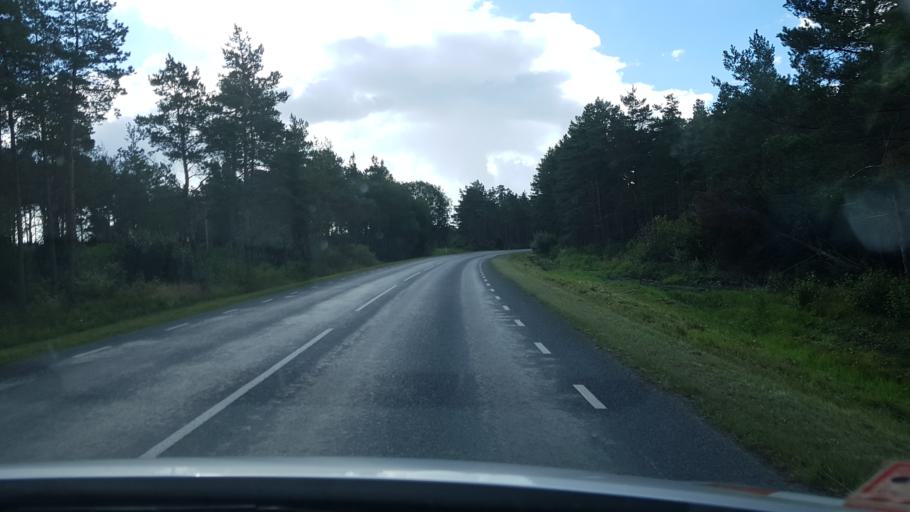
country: EE
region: Saare
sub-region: Kuressaare linn
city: Kuressaare
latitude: 58.3208
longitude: 22.4646
